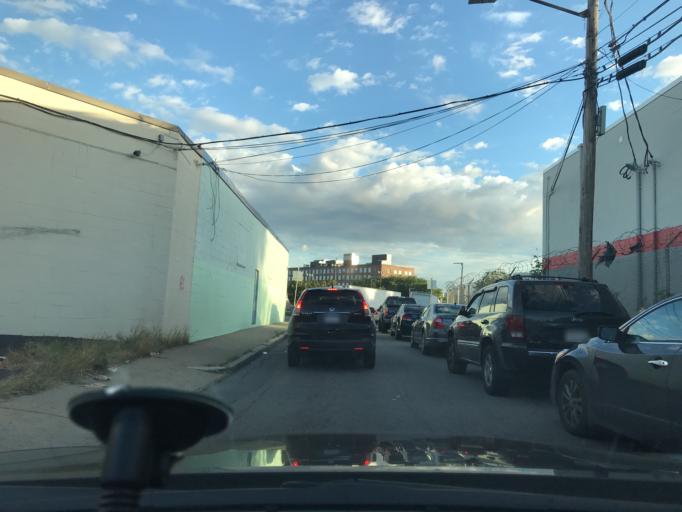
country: US
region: Massachusetts
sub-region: Suffolk County
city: South Boston
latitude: 42.3254
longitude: -71.0677
